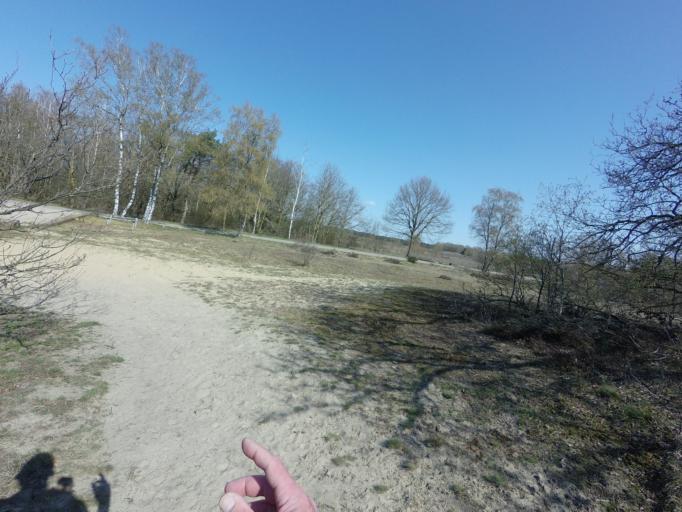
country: NL
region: Limburg
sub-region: Gemeente Bergen
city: Wellerlooi
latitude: 51.6036
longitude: 6.0694
